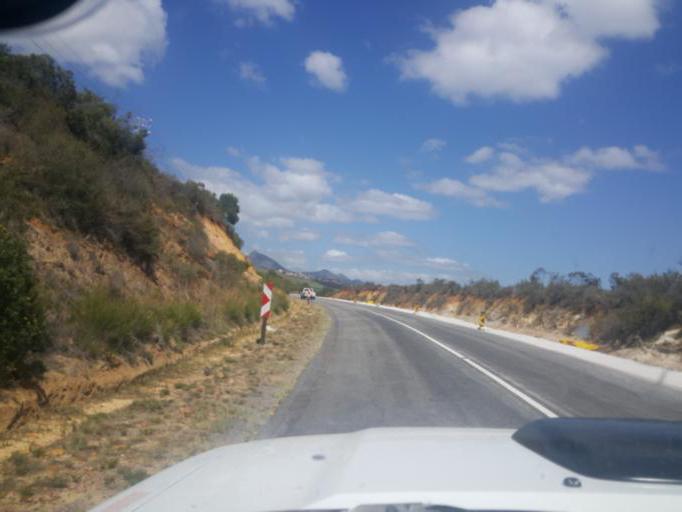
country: ZA
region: Eastern Cape
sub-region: Cacadu District Municipality
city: Kareedouw
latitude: -33.9491
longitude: 24.3359
